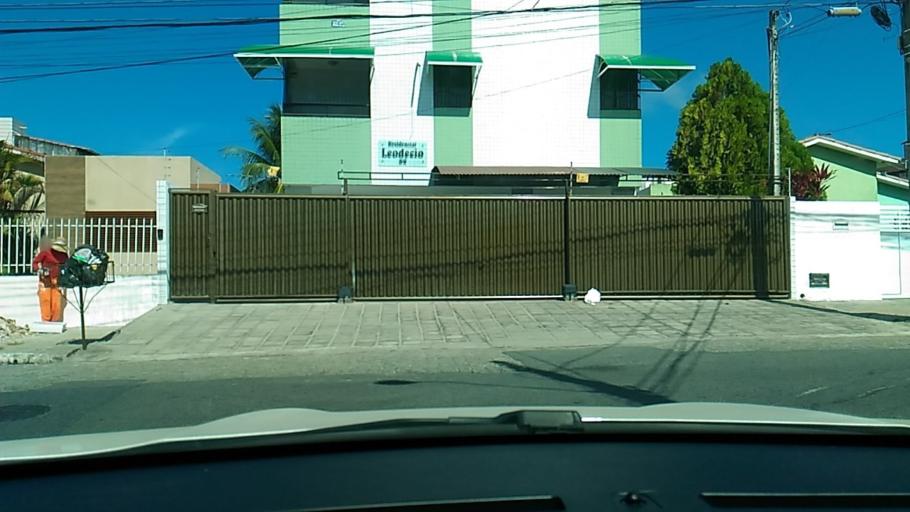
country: BR
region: Paraiba
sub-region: Joao Pessoa
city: Joao Pessoa
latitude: -7.1501
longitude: -34.8388
